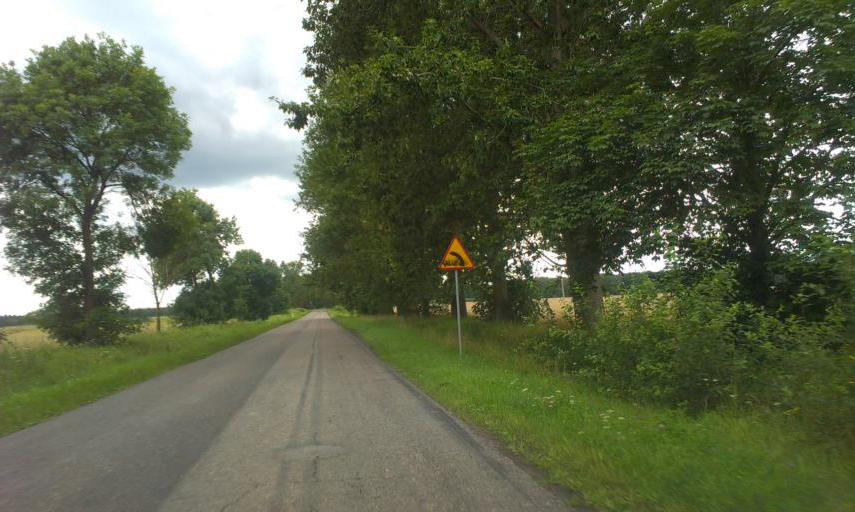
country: PL
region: West Pomeranian Voivodeship
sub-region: Powiat bialogardzki
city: Tychowo
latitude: 53.8885
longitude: 16.1883
